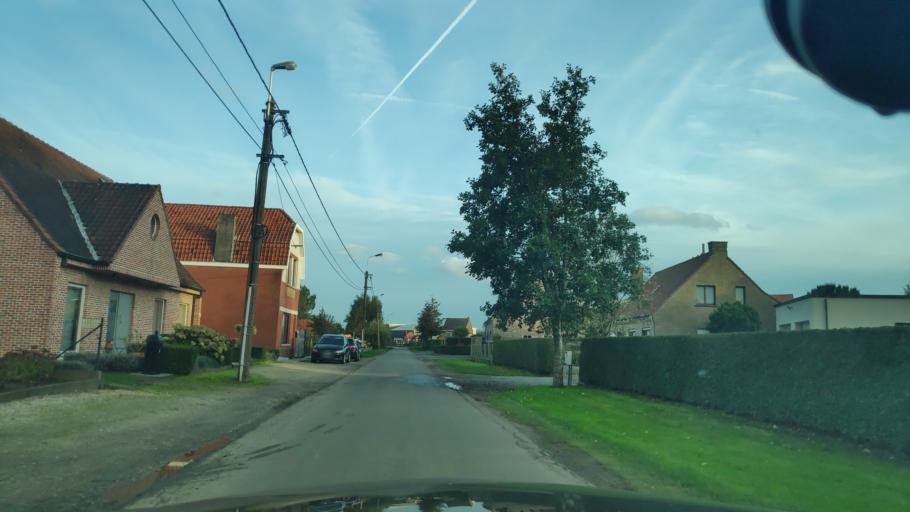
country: BE
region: Flanders
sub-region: Provincie Oost-Vlaanderen
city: Aalter
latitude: 51.1174
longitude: 3.4469
